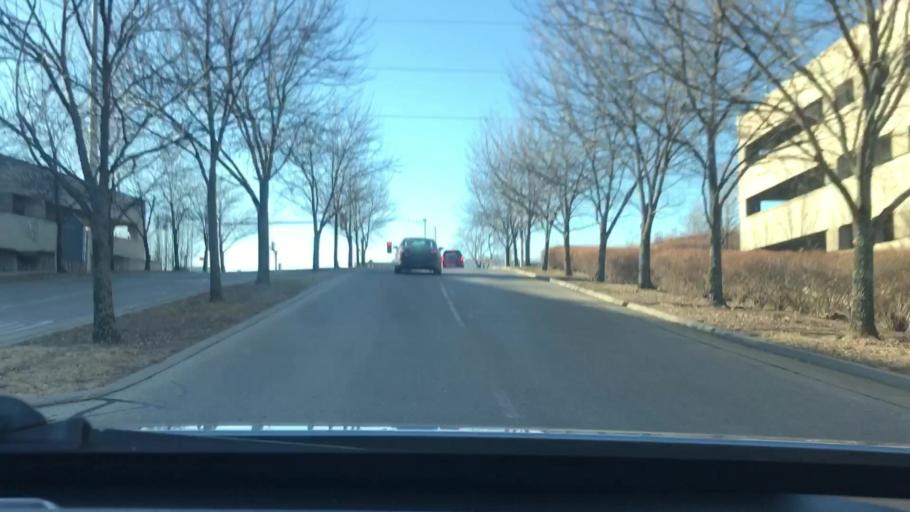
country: US
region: Kansas
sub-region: Johnson County
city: Leawood
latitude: 38.9191
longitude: -94.6596
